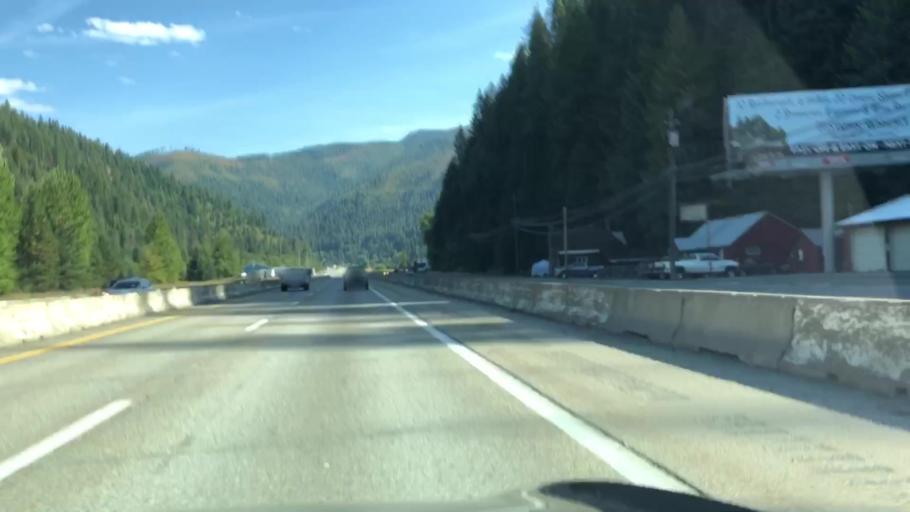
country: US
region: Idaho
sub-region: Shoshone County
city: Wallace
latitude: 47.4840
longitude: -115.9413
